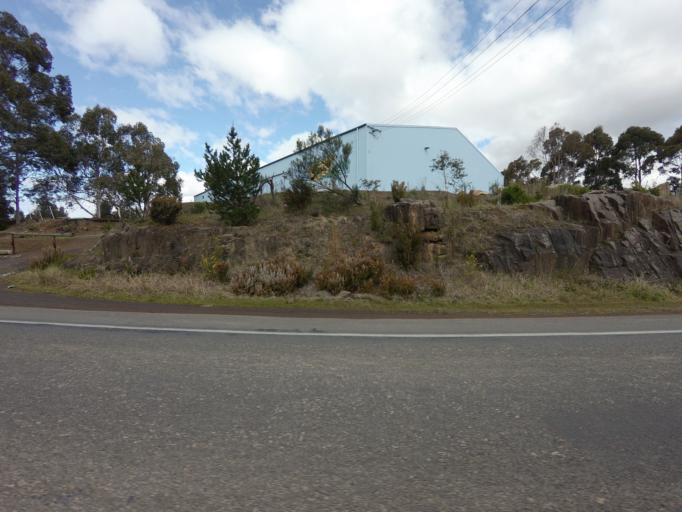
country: AU
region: Tasmania
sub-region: Huon Valley
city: Geeveston
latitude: -43.1563
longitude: 146.9568
